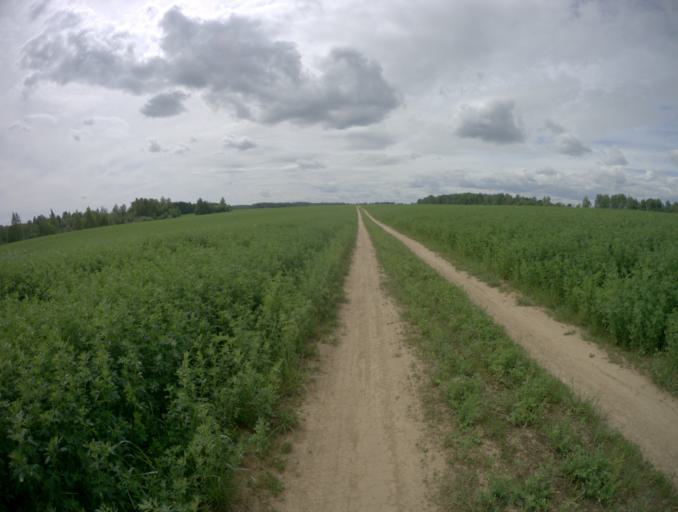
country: RU
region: Vladimir
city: Stavrovo
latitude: 56.2371
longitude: 39.9187
